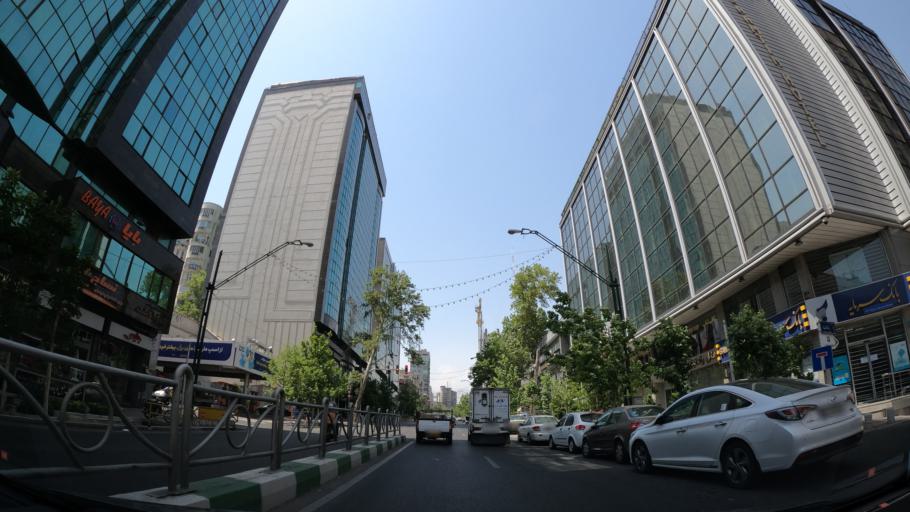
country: IR
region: Tehran
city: Tehran
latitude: 35.7321
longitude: 51.4114
